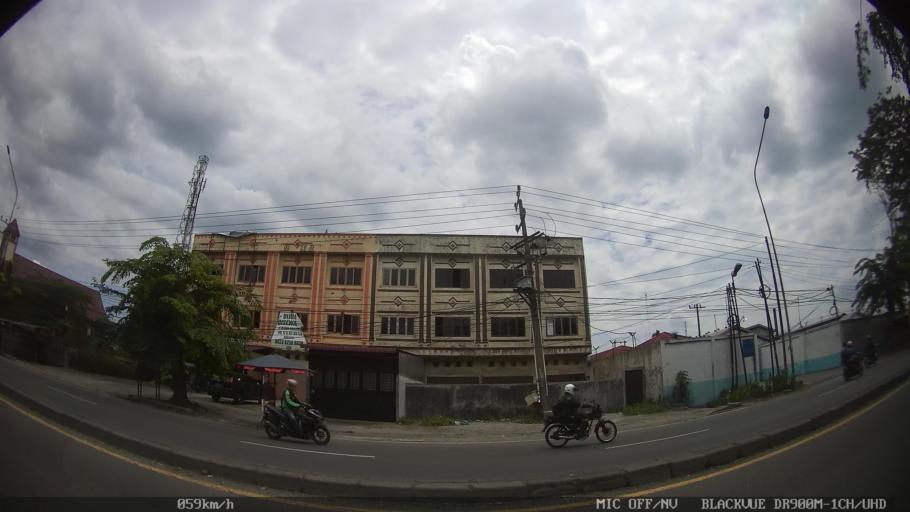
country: ID
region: North Sumatra
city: Sunggal
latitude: 3.5992
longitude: 98.5973
